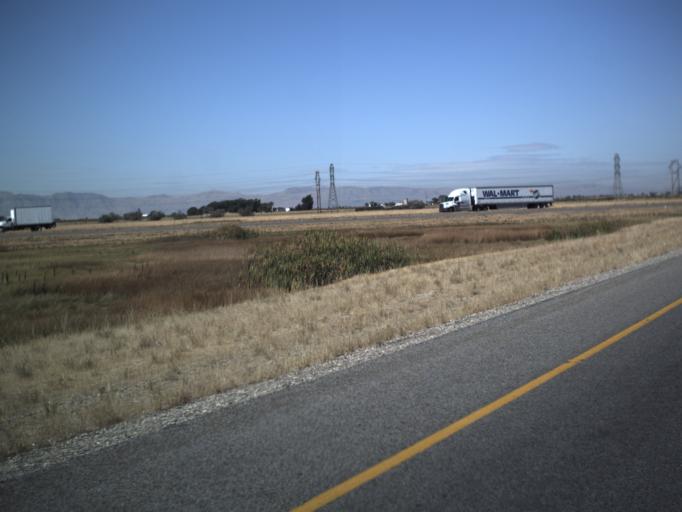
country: US
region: Utah
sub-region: Box Elder County
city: Brigham City
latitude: 41.5116
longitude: -112.0587
